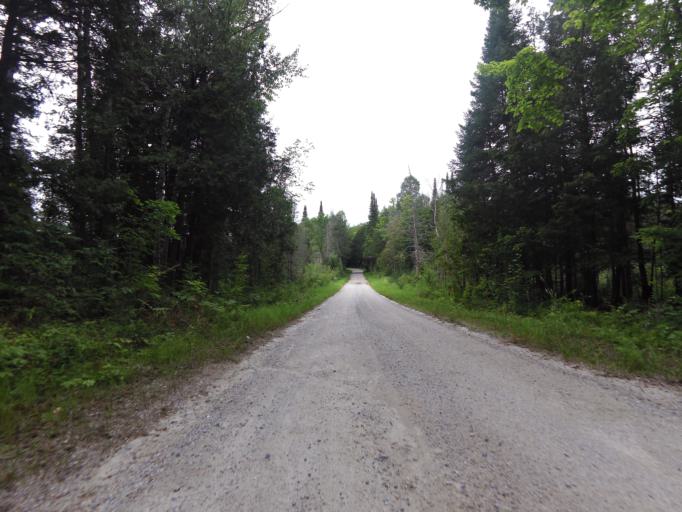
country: CA
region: Ontario
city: Perth
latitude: 44.8445
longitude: -76.5834
